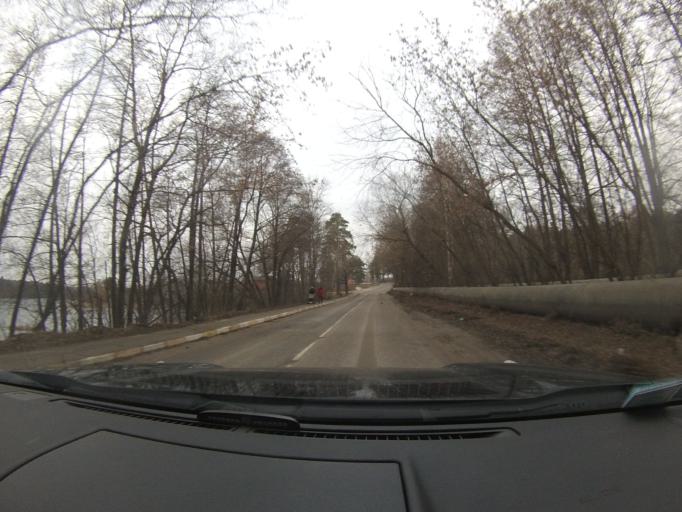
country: RU
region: Moskovskaya
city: Peski
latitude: 55.2642
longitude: 38.7595
